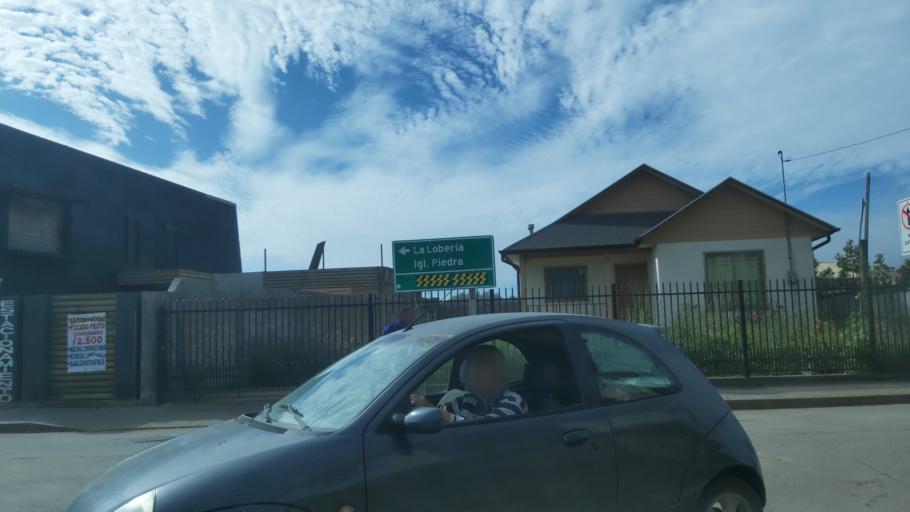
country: CL
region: Maule
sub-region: Provincia de Cauquenes
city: Cauquenes
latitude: -36.1342
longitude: -72.7991
